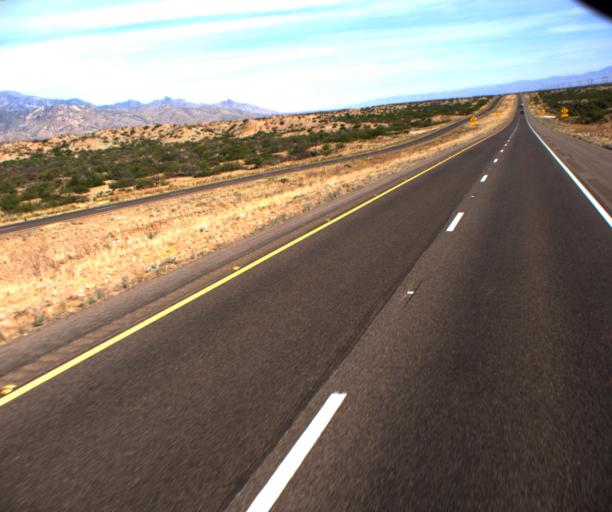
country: US
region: Arizona
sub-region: Graham County
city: Swift Trail Junction
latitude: 32.5802
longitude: -109.6822
